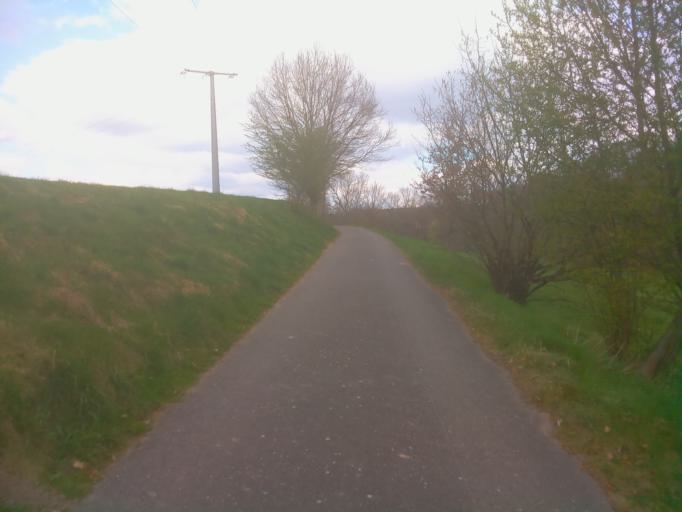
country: DE
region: Thuringia
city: Trobnitz
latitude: 50.8346
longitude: 11.7339
